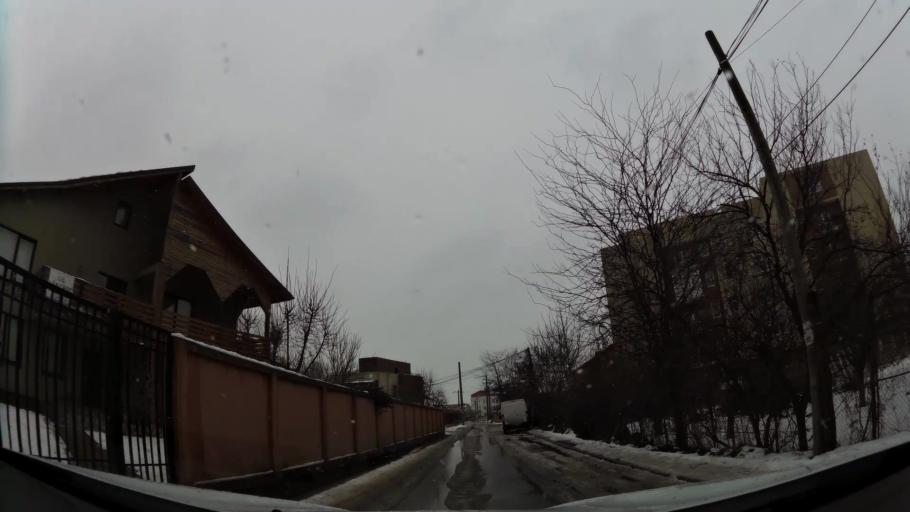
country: RO
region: Ilfov
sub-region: Comuna Chiajna
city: Rosu
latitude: 44.4047
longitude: 26.0115
